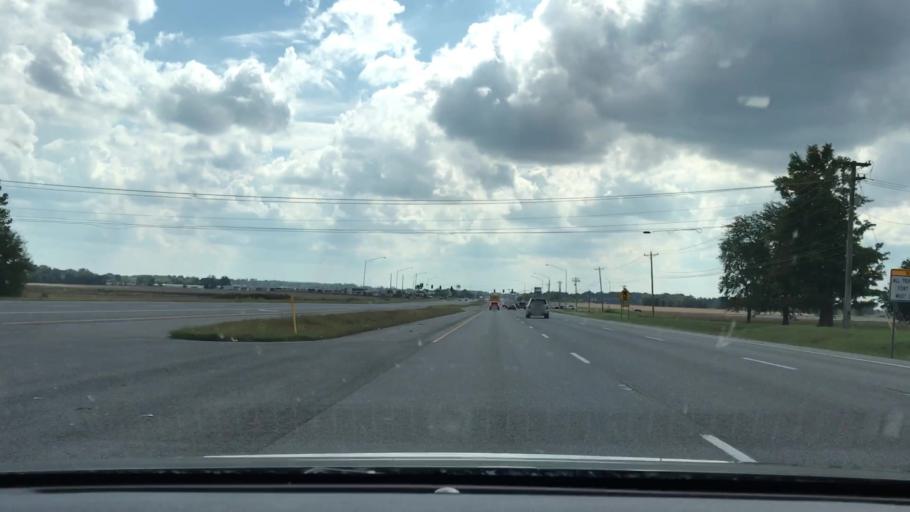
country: US
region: Kentucky
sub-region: Christian County
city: Oak Grove
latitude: 36.6789
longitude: -87.4473
